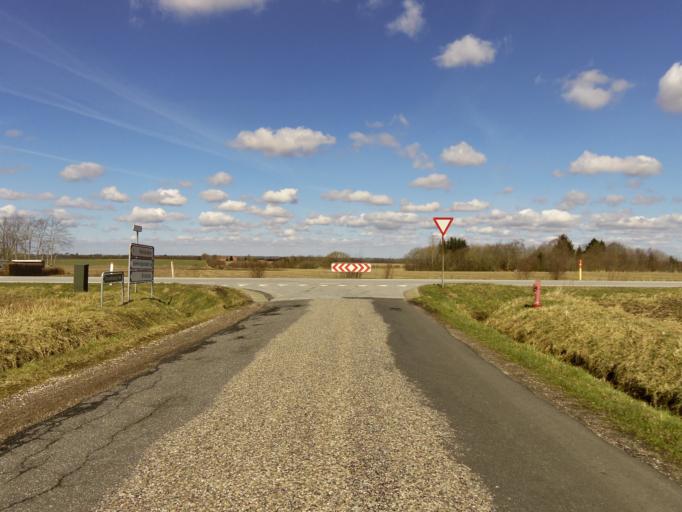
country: DK
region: South Denmark
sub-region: Tonder Kommune
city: Toftlund
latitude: 55.1917
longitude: 9.0960
